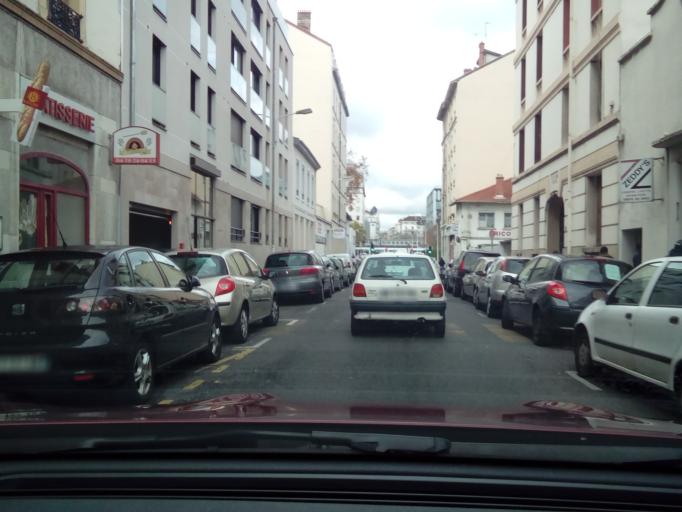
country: FR
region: Rhone-Alpes
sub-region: Departement du Rhone
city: Villeurbanne
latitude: 45.7664
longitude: 4.8647
